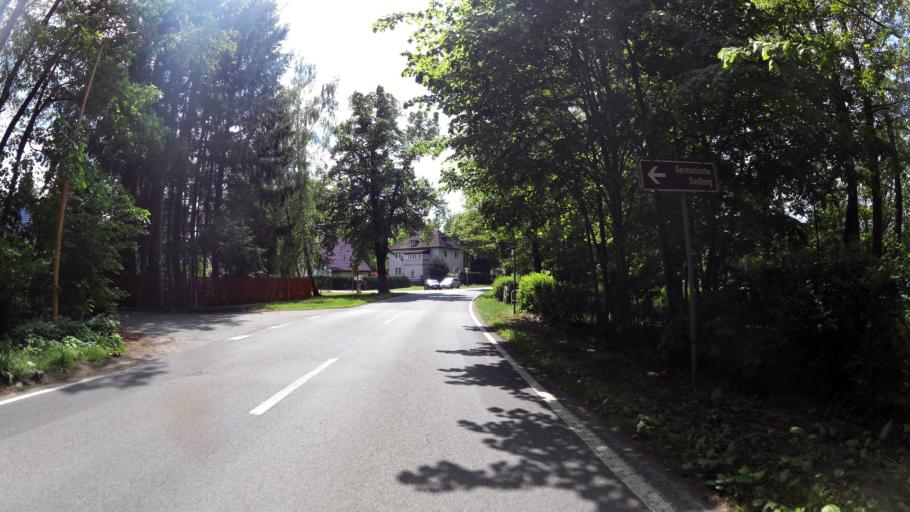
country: DE
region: Brandenburg
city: Gross Koris
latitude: 52.1699
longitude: 13.6973
